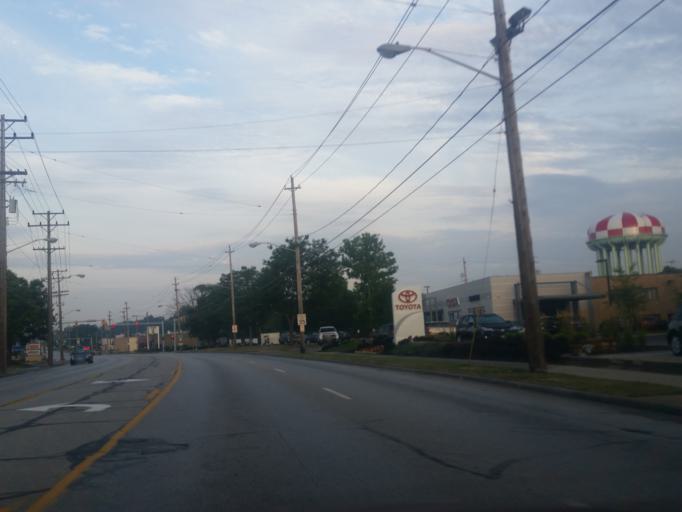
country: US
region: Ohio
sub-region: Cuyahoga County
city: North Olmsted
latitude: 41.4177
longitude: -81.9198
